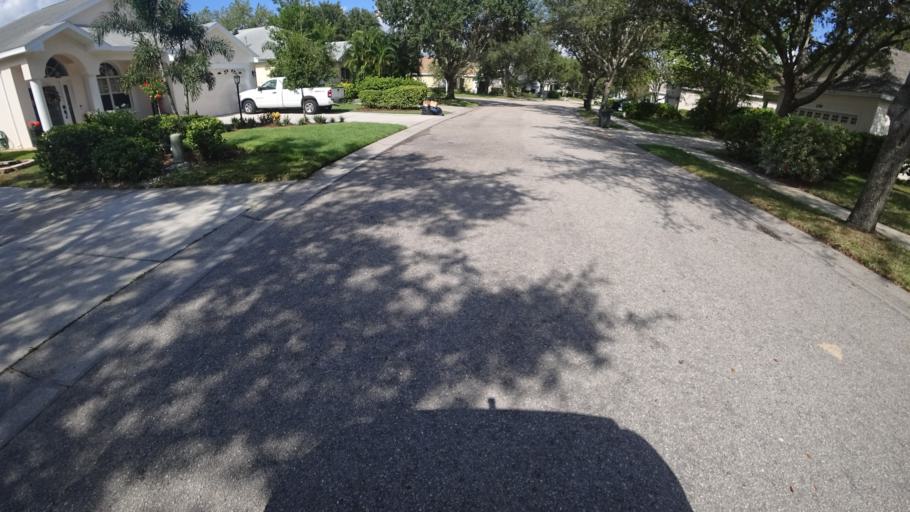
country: US
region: Florida
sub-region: Sarasota County
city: The Meadows
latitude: 27.4307
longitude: -82.4186
